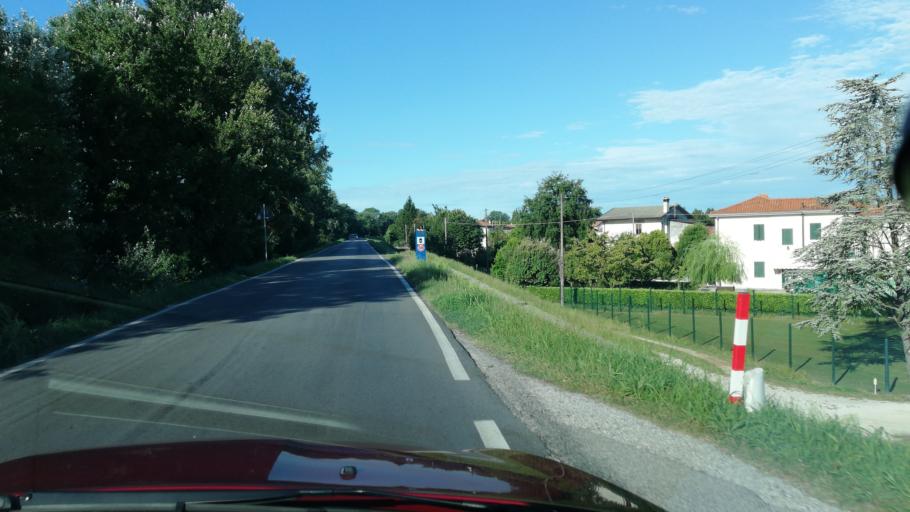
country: IT
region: Veneto
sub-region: Provincia di Venezia
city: Eraclea
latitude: 45.5756
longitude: 12.6827
